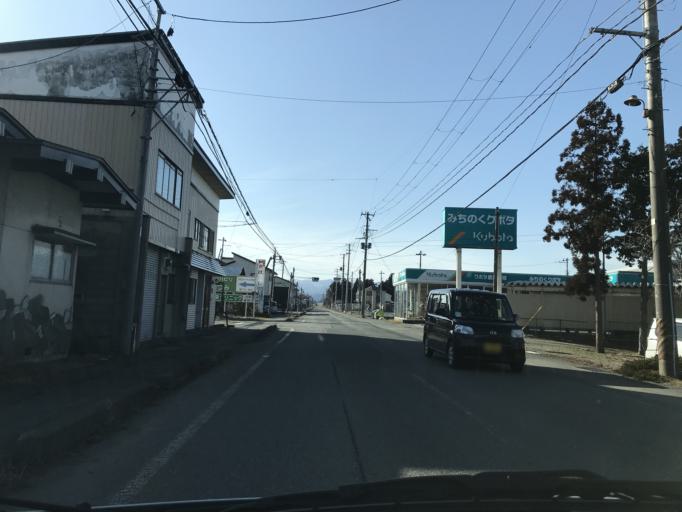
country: JP
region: Iwate
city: Kitakami
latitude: 39.3017
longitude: 141.0307
